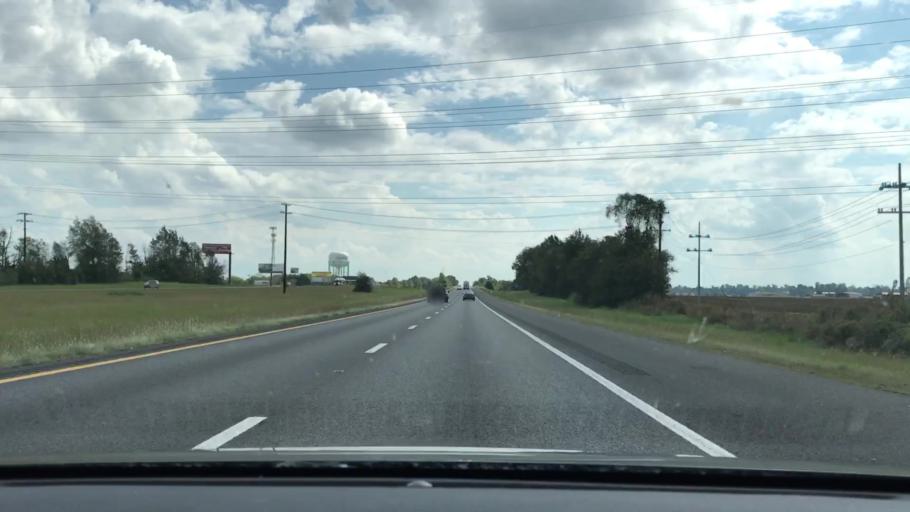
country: US
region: Tennessee
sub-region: Montgomery County
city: Clarksville
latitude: 36.5940
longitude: -87.2791
